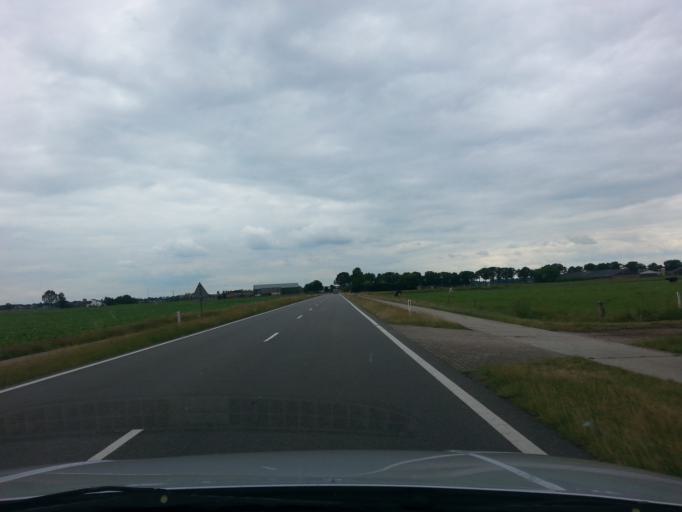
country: NL
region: North Brabant
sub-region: Gemeente Boxmeer
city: Overloon
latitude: 51.5116
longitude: 5.8861
